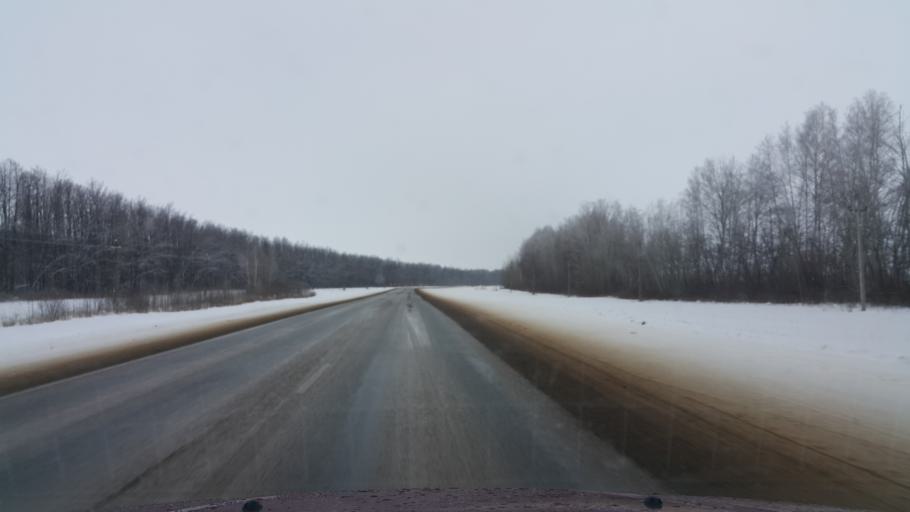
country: RU
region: Tambov
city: Bokino
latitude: 52.5947
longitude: 41.4449
